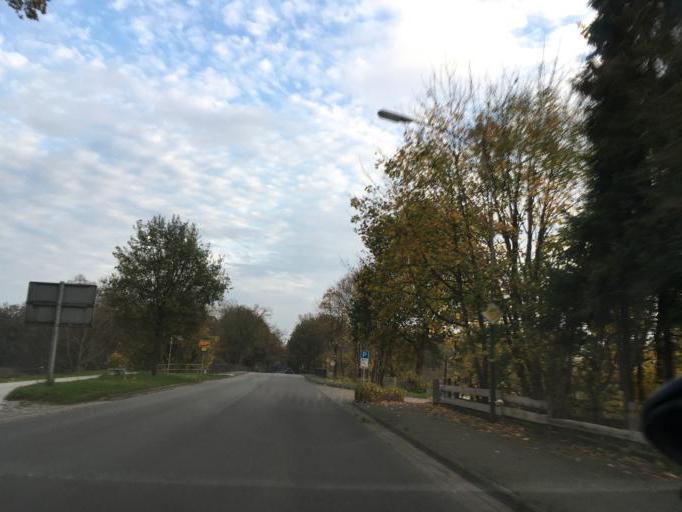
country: DE
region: Lower Saxony
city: Hambuhren
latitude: 52.6954
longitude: 9.9832
